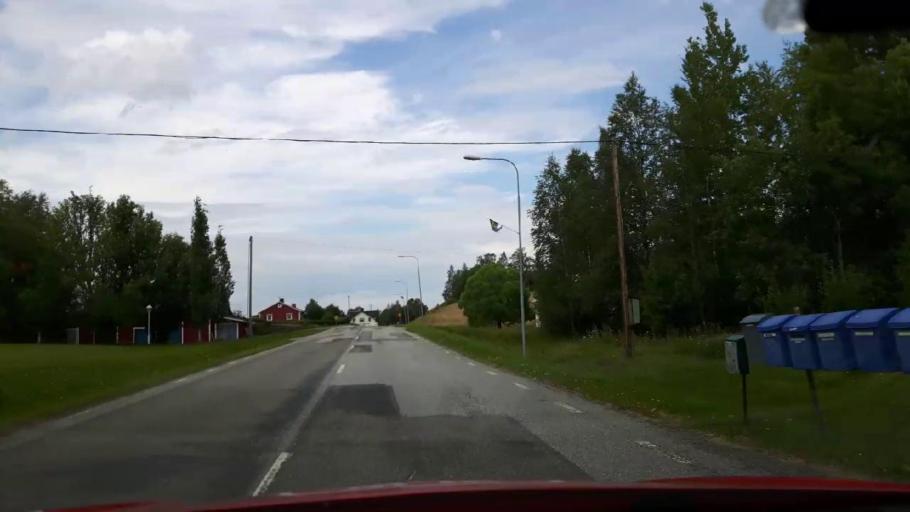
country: SE
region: Jaemtland
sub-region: Stroemsunds Kommun
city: Stroemsund
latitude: 64.4305
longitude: 15.5967
